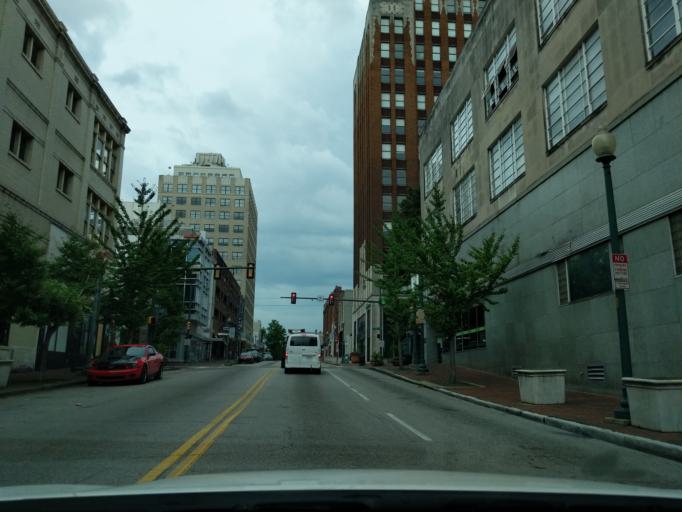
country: US
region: Tennessee
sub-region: Shelby County
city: Memphis
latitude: 35.1431
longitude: -90.0530
